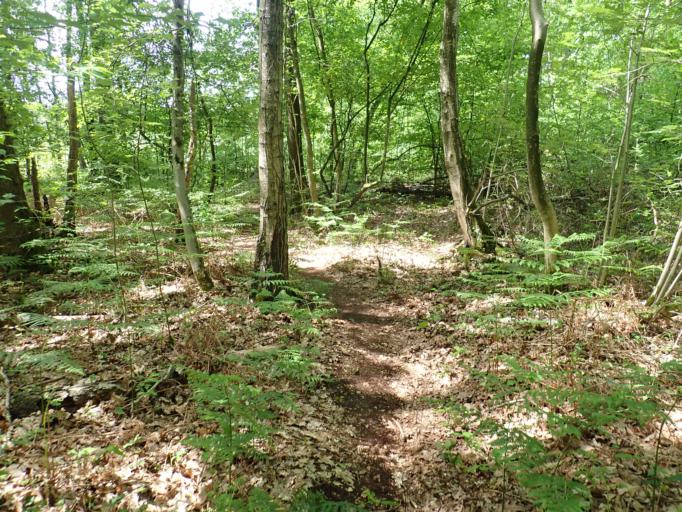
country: BE
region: Flanders
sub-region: Provincie Antwerpen
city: Herselt
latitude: 51.0647
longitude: 4.8707
